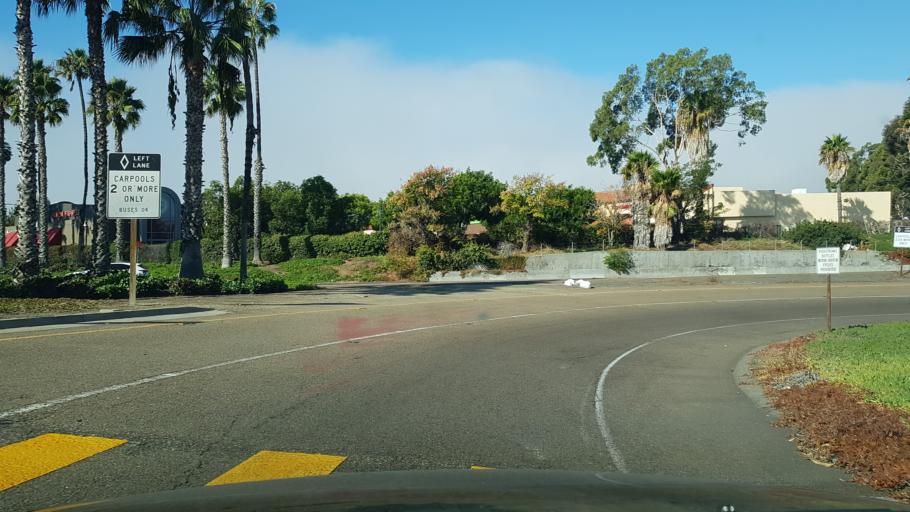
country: US
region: California
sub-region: San Diego County
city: Oceanside
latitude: 33.1997
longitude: -117.3733
